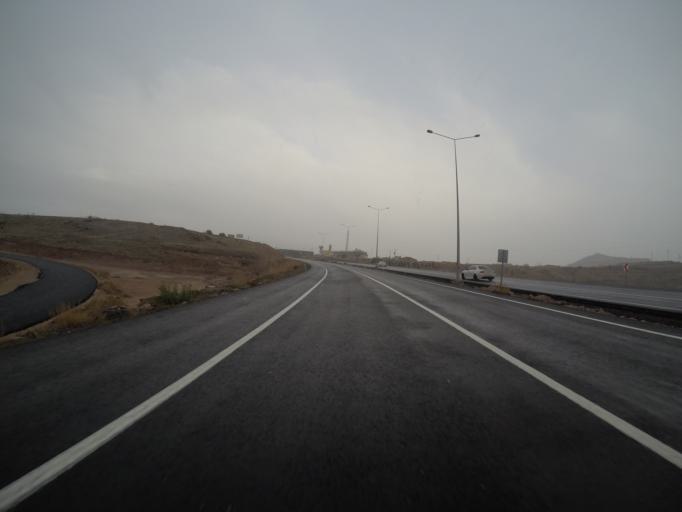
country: TR
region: Nevsehir
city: Nevsehir
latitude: 38.6732
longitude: 34.7568
